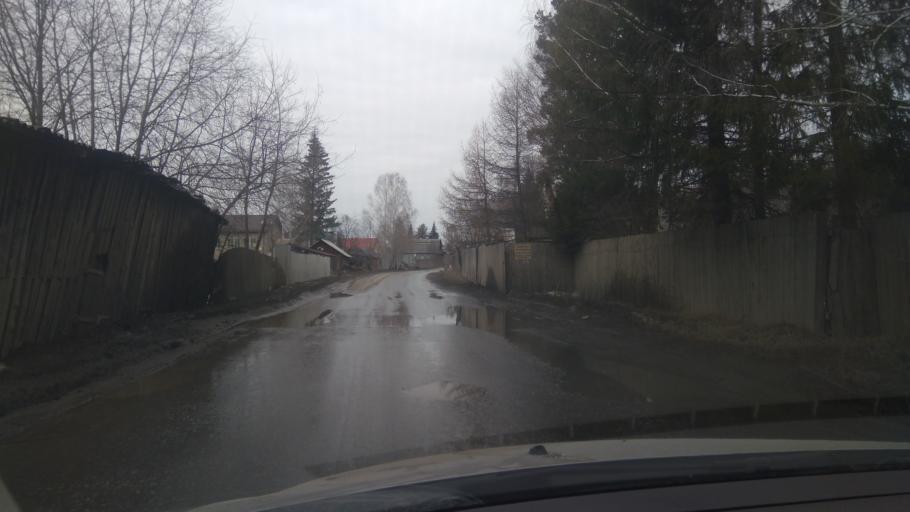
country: RU
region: Sverdlovsk
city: Severka
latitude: 56.8476
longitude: 60.3834
